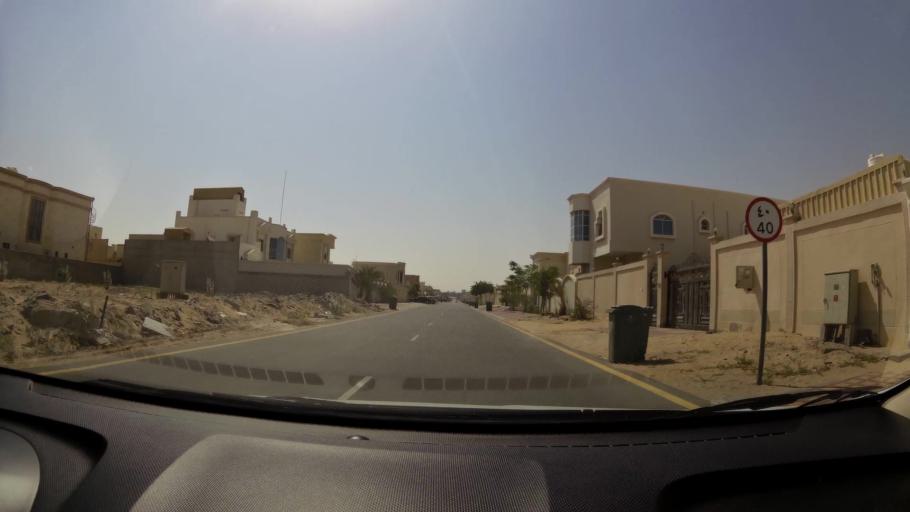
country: AE
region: Ajman
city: Ajman
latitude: 25.4131
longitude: 55.5497
